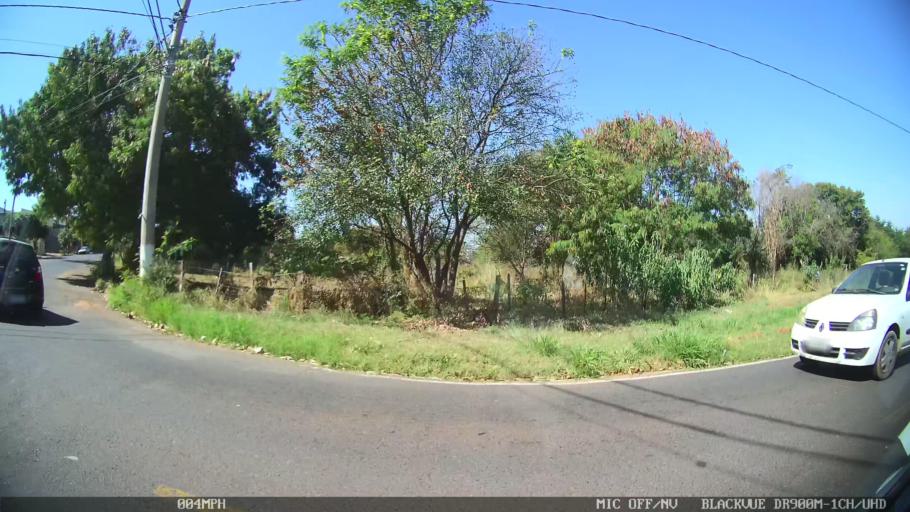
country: BR
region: Sao Paulo
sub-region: Sao Jose Do Rio Preto
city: Sao Jose do Rio Preto
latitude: -20.7694
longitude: -49.3983
